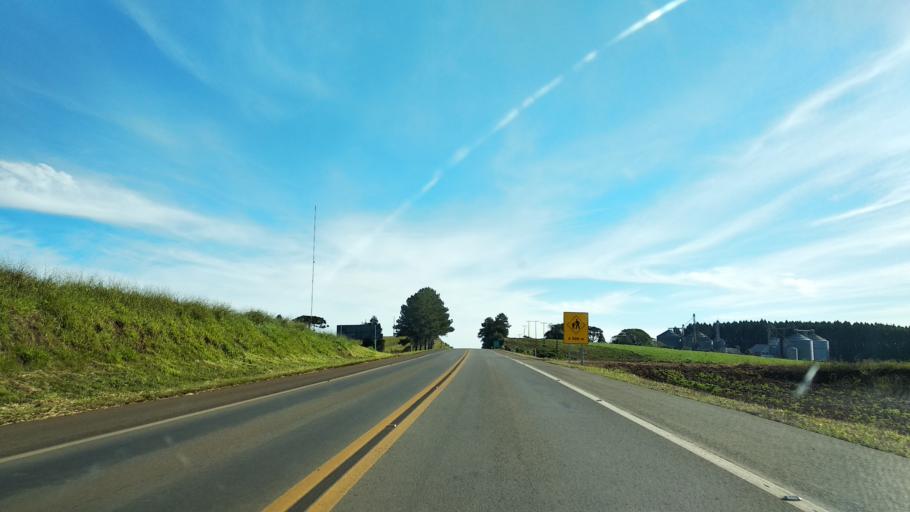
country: BR
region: Santa Catarina
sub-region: Celso Ramos
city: Celso Ramos
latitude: -27.5278
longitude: -51.3803
